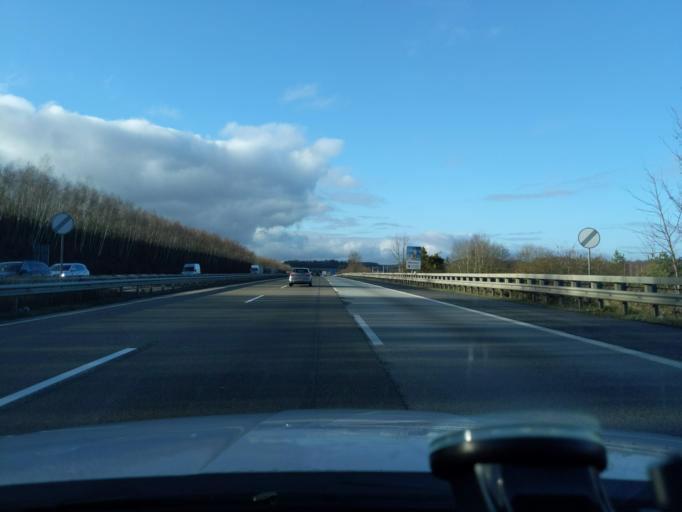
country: DE
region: Rheinland-Pfalz
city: Gorgeshausen
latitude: 50.4124
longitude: 7.9641
